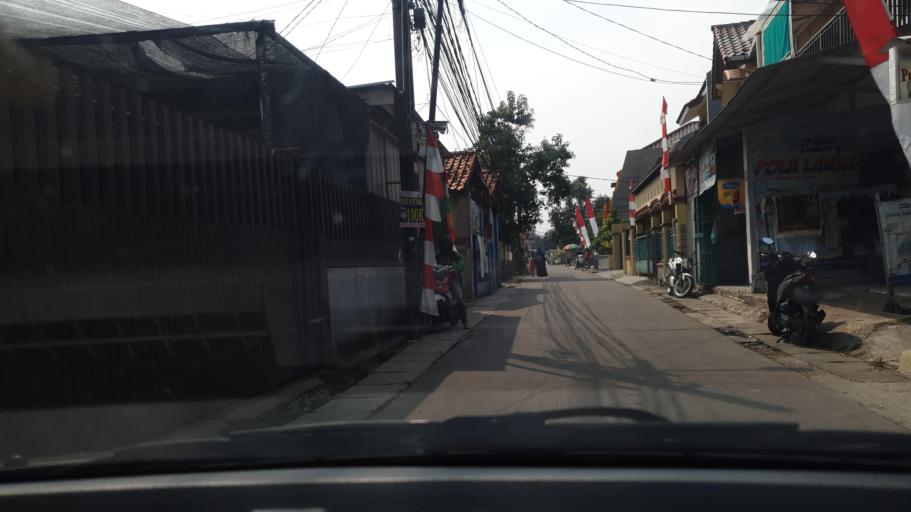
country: ID
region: West Java
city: Pamulang
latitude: -6.3322
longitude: 106.7674
